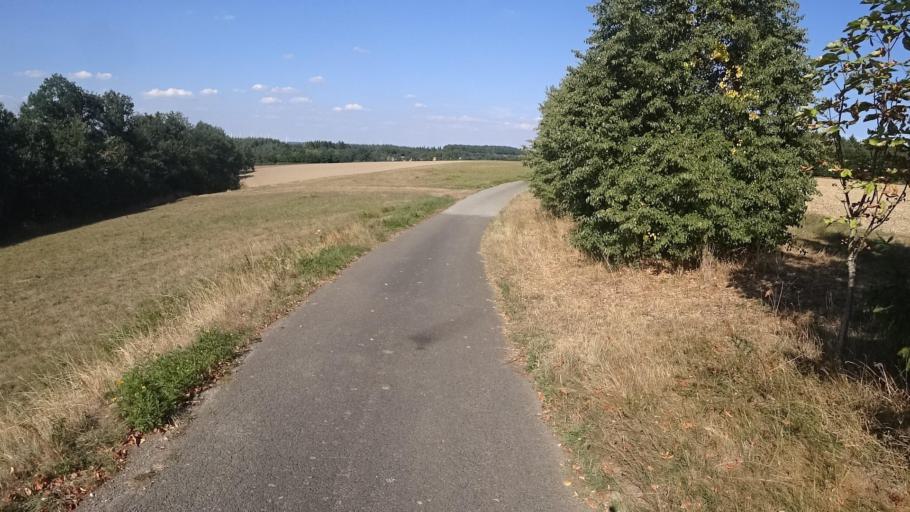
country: DE
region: Rheinland-Pfalz
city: Belgweiler
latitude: 49.9475
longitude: 7.4904
